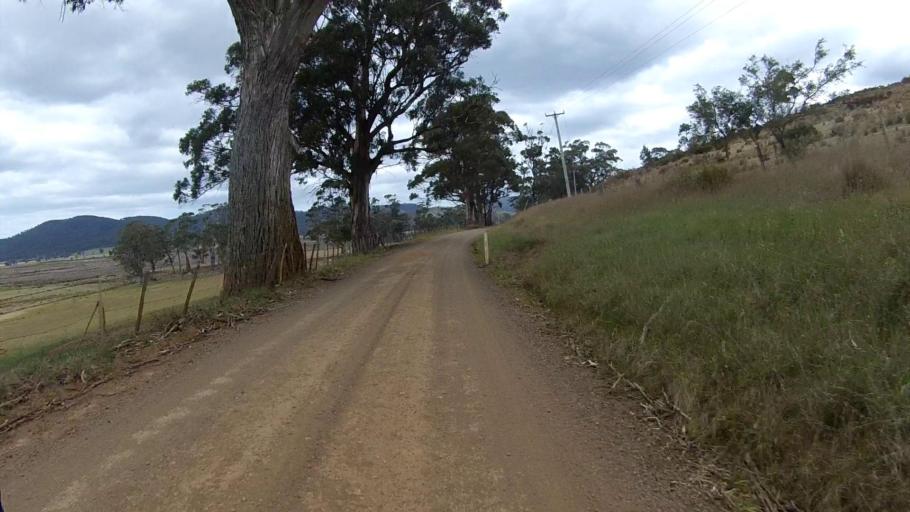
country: AU
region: Tasmania
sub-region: Sorell
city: Sorell
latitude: -42.6310
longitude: 147.9279
